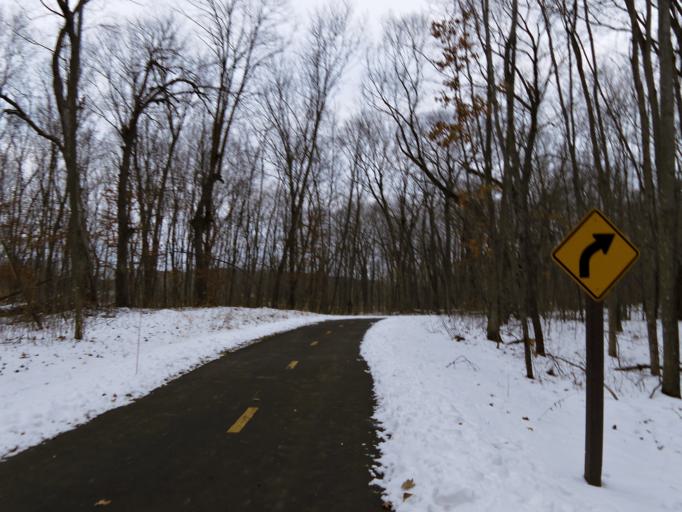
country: US
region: Minnesota
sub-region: Scott County
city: Prior Lake
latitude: 44.7137
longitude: -93.4729
